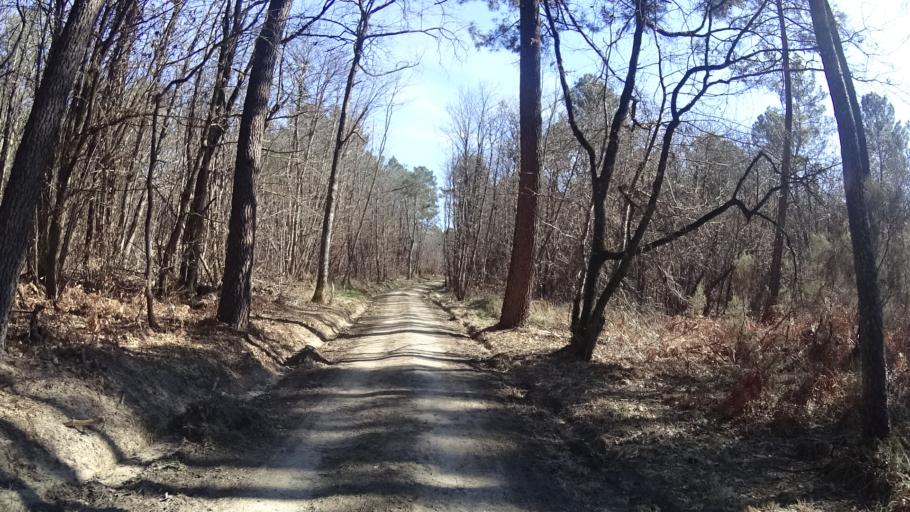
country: FR
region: Aquitaine
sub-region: Departement de la Dordogne
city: Riberac
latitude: 45.1940
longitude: 0.3126
